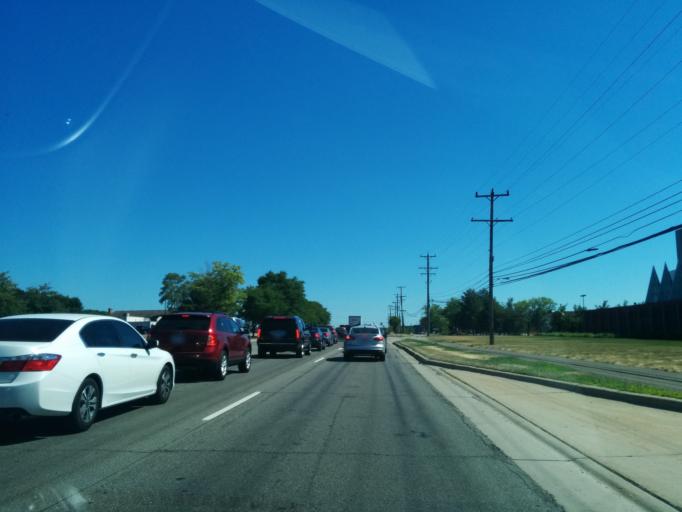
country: US
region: Michigan
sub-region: Oakland County
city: Farmington Hills
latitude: 42.5025
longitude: -83.3589
